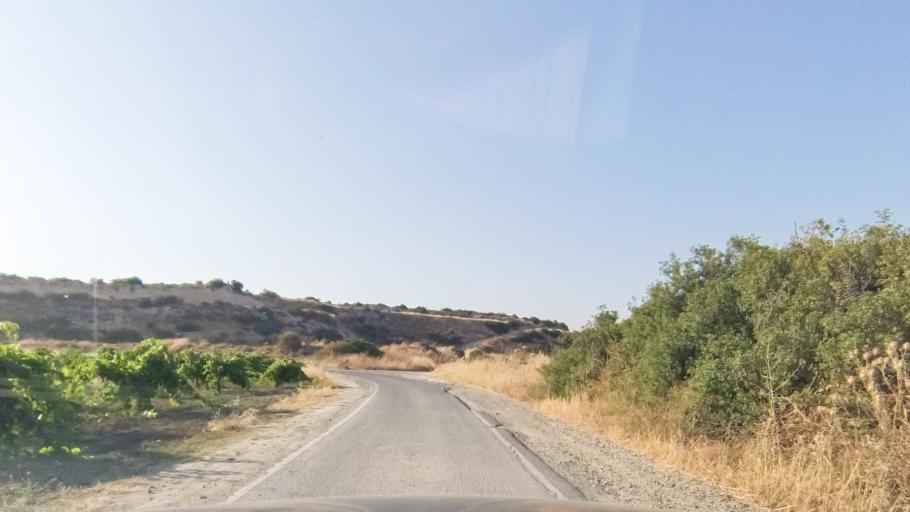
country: CY
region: Limassol
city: Pissouri
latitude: 34.6733
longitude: 32.7668
